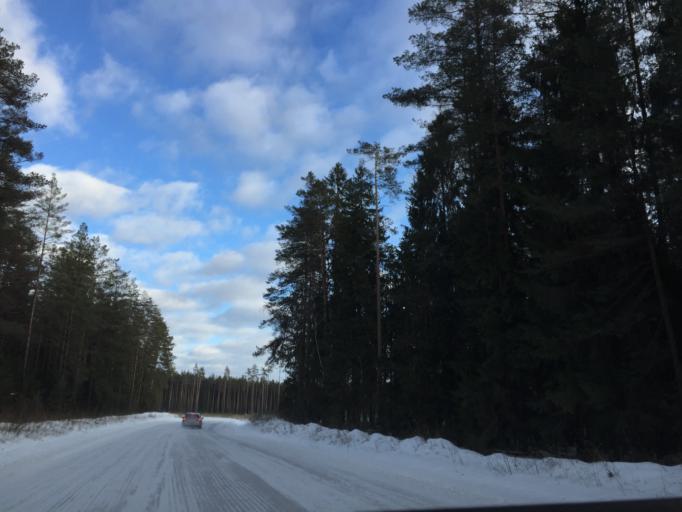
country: LV
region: Ogre
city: Jumprava
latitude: 56.5774
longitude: 24.9458
